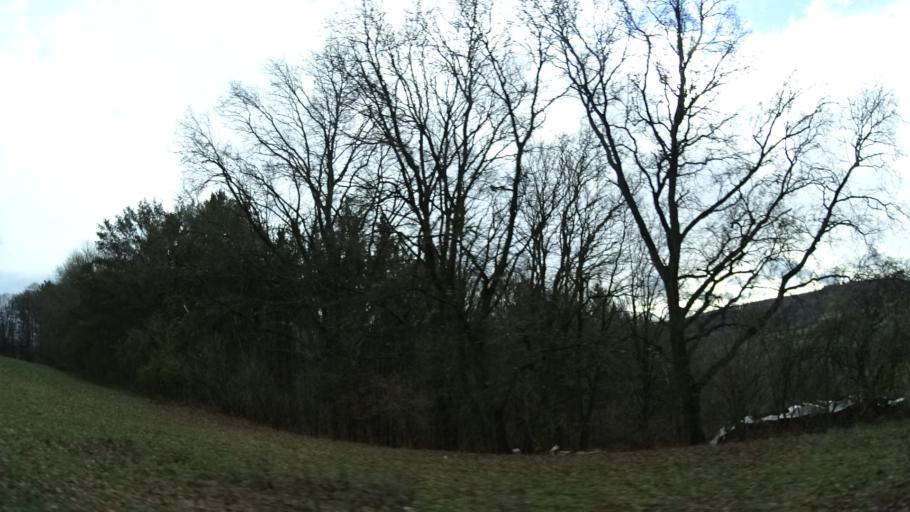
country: DE
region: Thuringia
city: Stepfershausen
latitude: 50.5607
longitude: 10.2950
